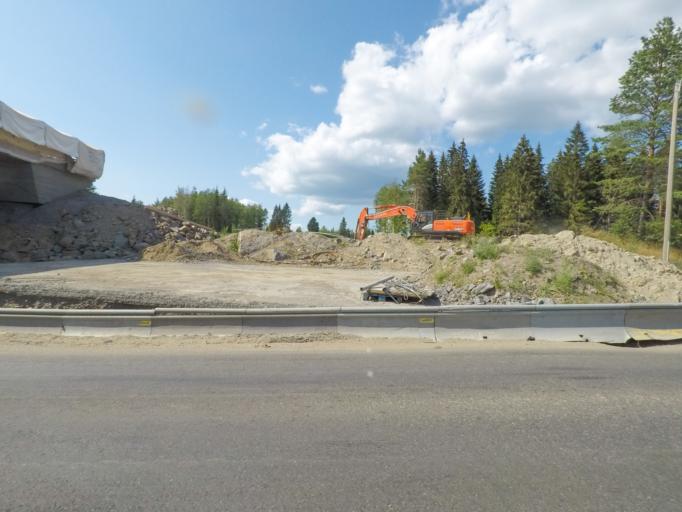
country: FI
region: Southern Savonia
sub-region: Mikkeli
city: Mikkeli
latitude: 61.7023
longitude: 27.3203
